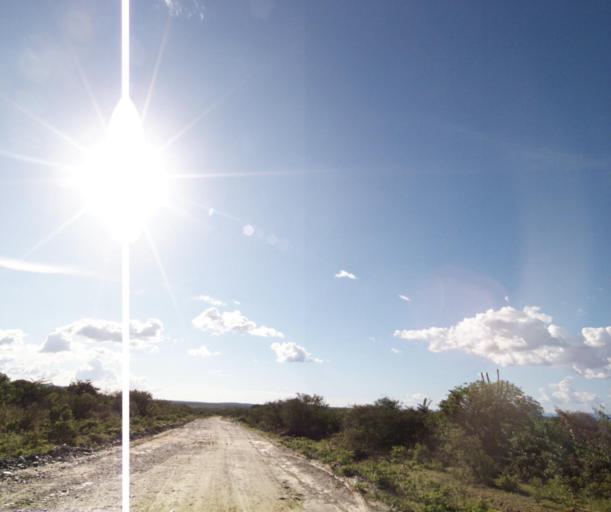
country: BR
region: Bahia
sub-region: Tanhacu
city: Tanhacu
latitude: -14.1857
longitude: -40.9928
